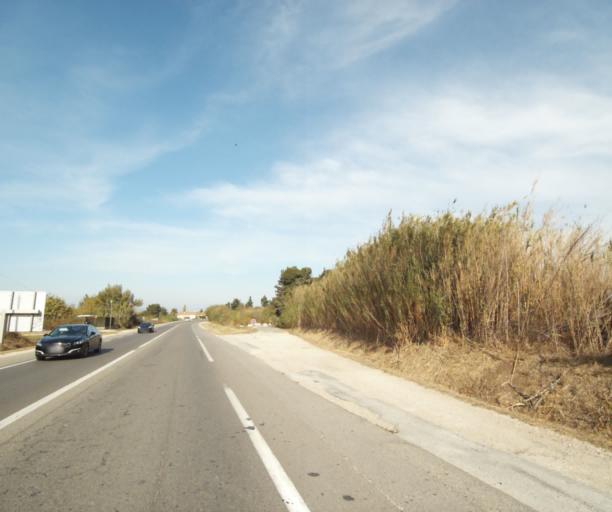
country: FR
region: Provence-Alpes-Cote d'Azur
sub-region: Departement des Bouches-du-Rhone
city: Chateauneuf-les-Martigues
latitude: 43.3838
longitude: 5.1924
